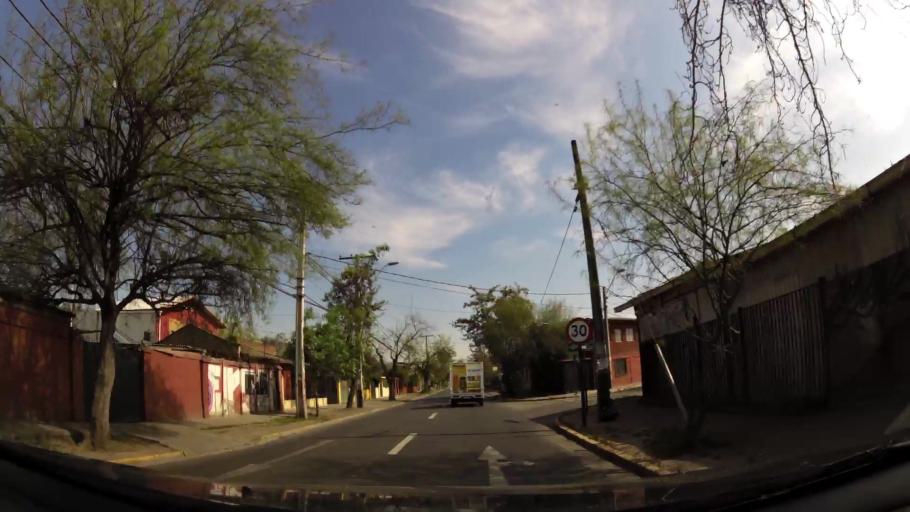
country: CL
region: Santiago Metropolitan
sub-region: Provincia de Santiago
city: Santiago
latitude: -33.4014
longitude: -70.6457
